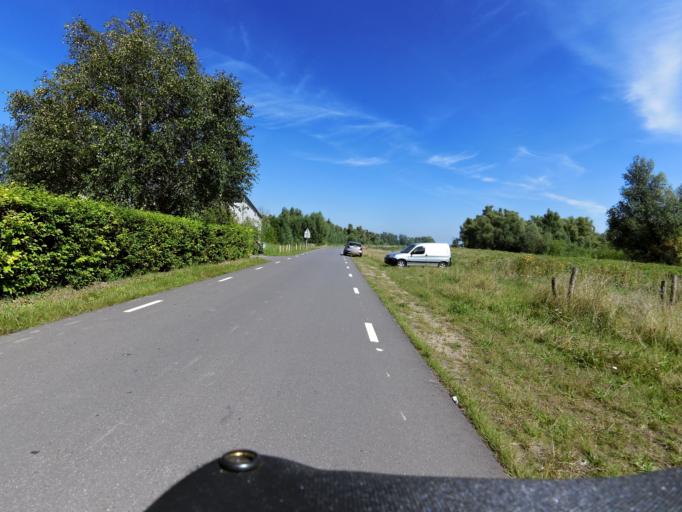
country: NL
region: South Holland
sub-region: Gemeente Sliedrecht
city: Sliedrecht
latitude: 51.7664
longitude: 4.7798
